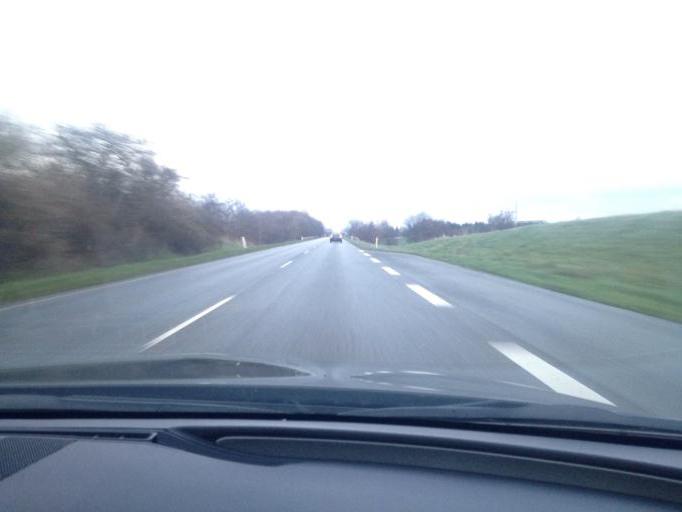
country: DK
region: South Denmark
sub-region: Kolding Kommune
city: Kolding
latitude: 55.5590
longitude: 9.4890
